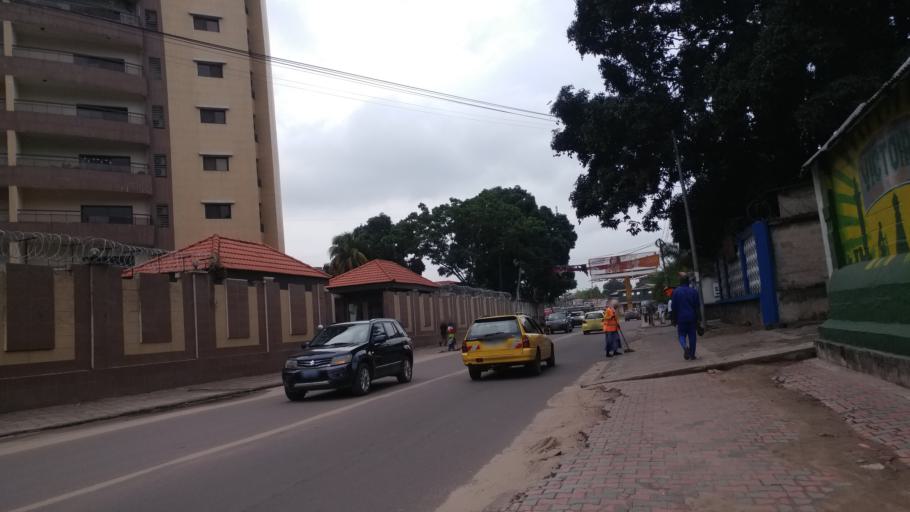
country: CD
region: Kinshasa
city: Kinshasa
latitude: -4.3225
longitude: 15.2772
